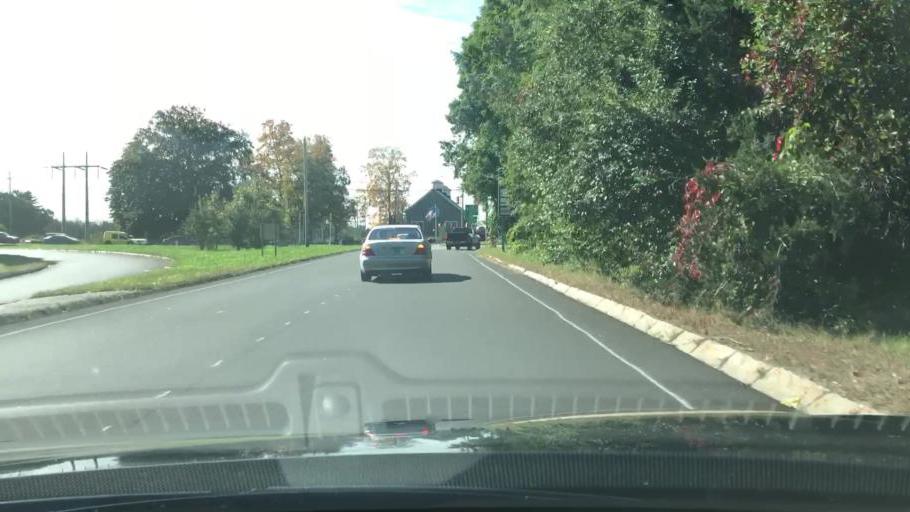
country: US
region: Massachusetts
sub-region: Essex County
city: Methuen
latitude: 42.7343
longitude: -71.1910
